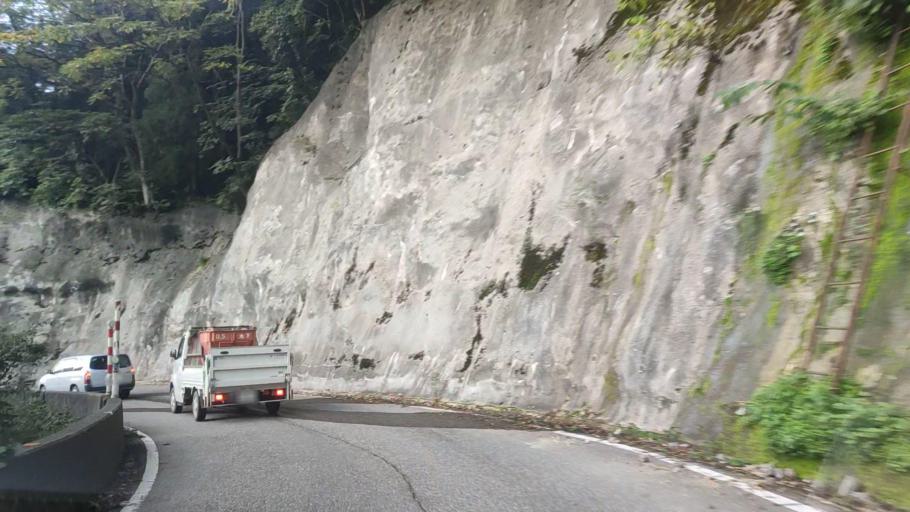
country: JP
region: Toyama
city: Nanto-shi
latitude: 36.5534
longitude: 137.0118
